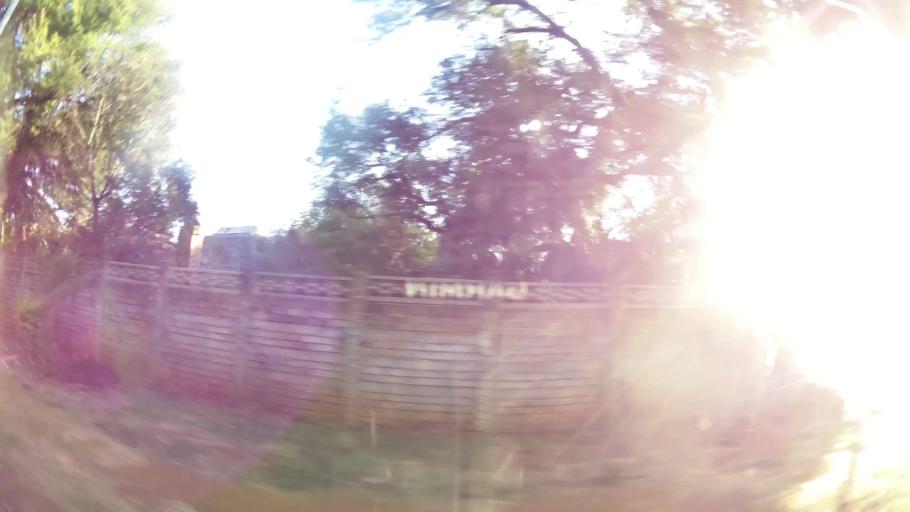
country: ZA
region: Gauteng
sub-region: City of Tshwane Metropolitan Municipality
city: Centurion
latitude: -25.8547
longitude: 28.1508
